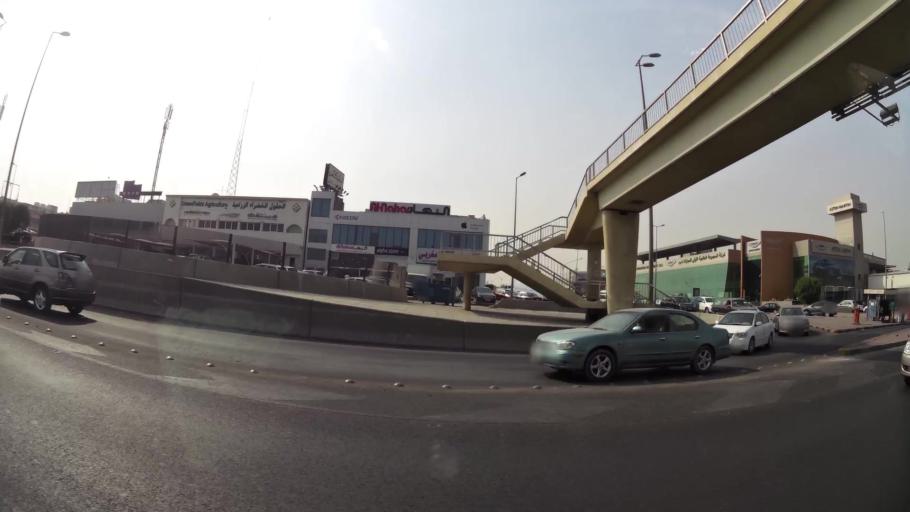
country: KW
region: Al Asimah
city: Ar Rabiyah
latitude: 29.3085
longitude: 47.9436
